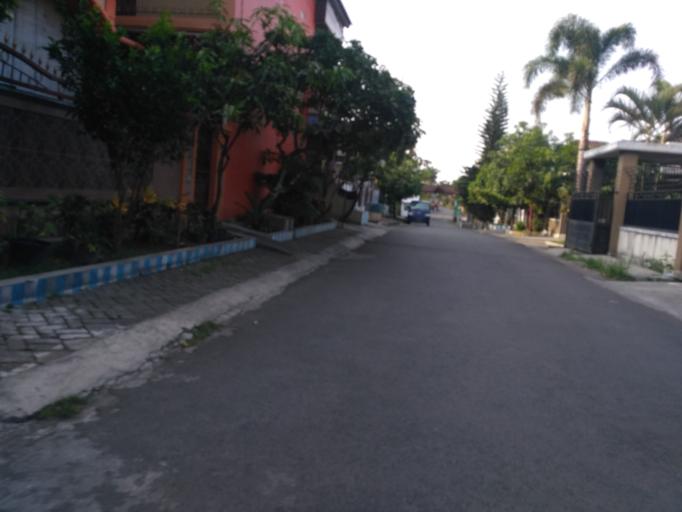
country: ID
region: East Java
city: Malang
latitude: -7.9373
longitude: 112.6309
